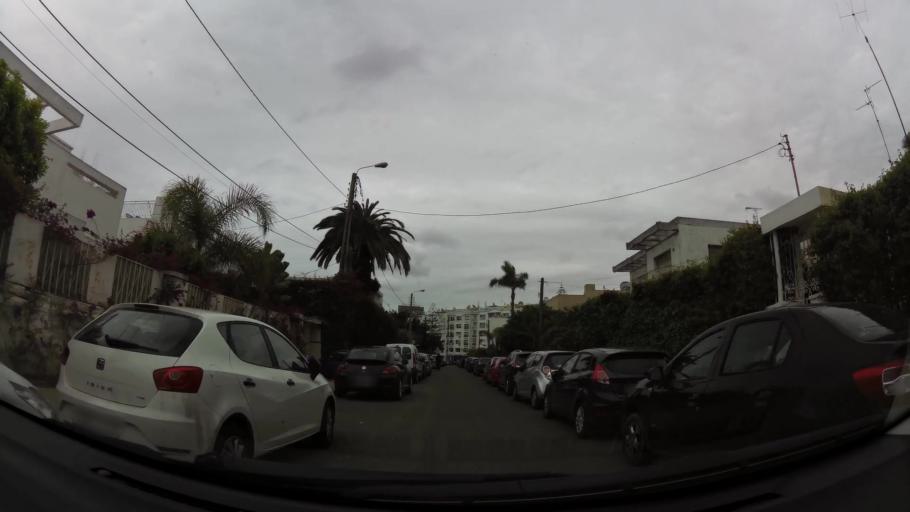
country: MA
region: Grand Casablanca
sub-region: Casablanca
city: Casablanca
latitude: 33.5867
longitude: -7.6471
